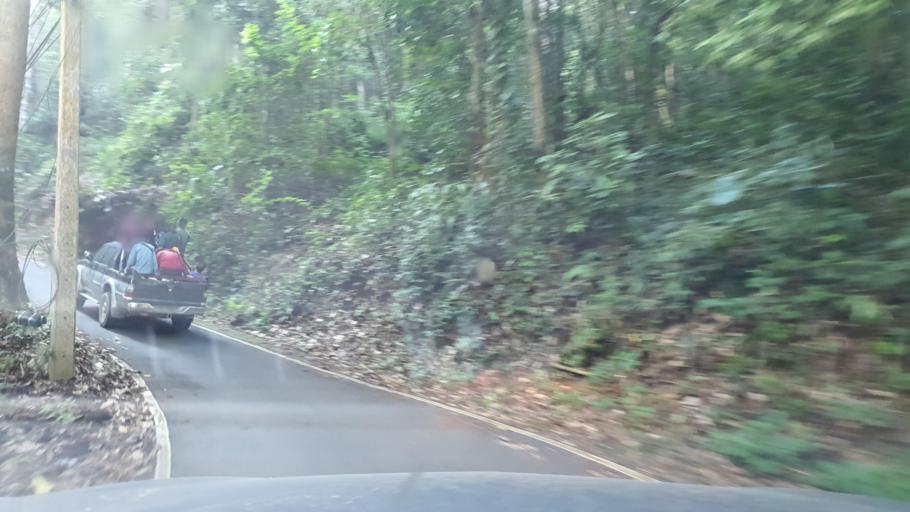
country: TH
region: Chiang Mai
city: Chiang Mai
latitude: 18.8242
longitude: 98.8909
